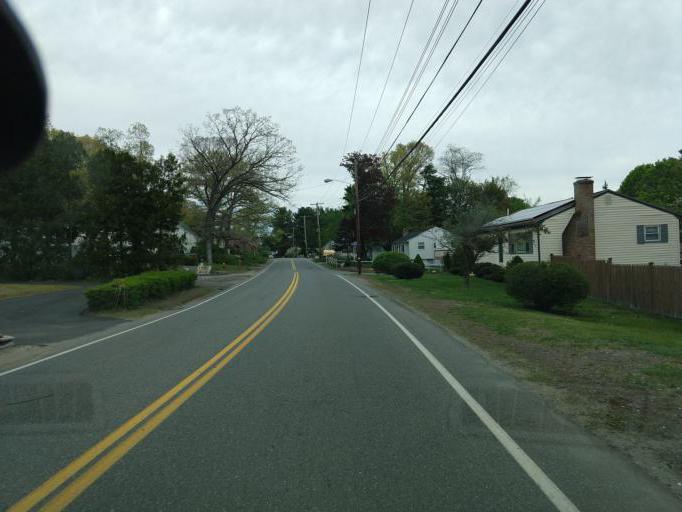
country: US
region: Massachusetts
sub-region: Middlesex County
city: Tewksbury
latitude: 42.6064
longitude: -71.1894
